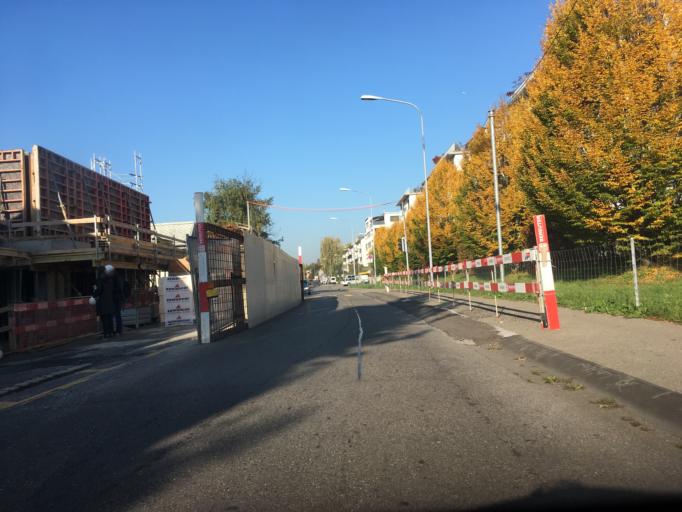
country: CH
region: Zurich
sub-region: Bezirk Zuerich
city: Zuerich (Kreis 10) / Hoengg
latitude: 47.3987
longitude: 8.5004
